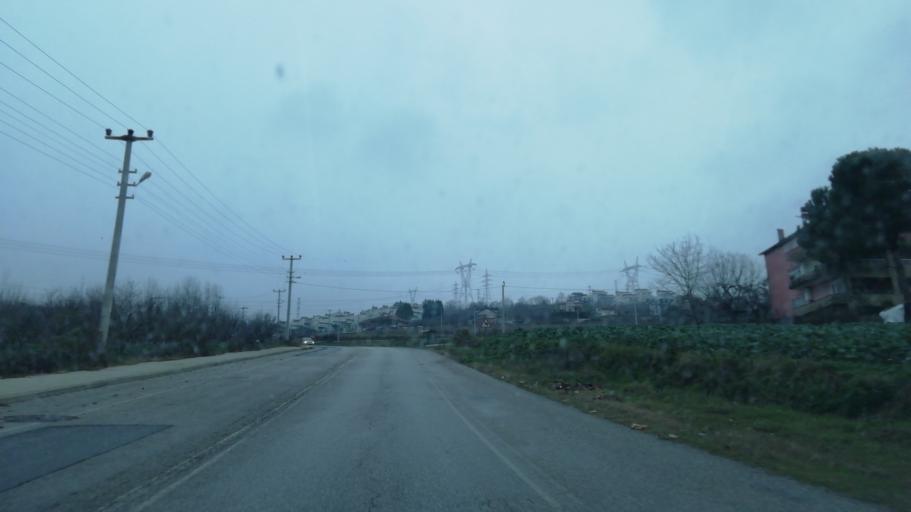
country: TR
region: Sakarya
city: Kazimpasa
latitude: 40.7411
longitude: 30.3081
